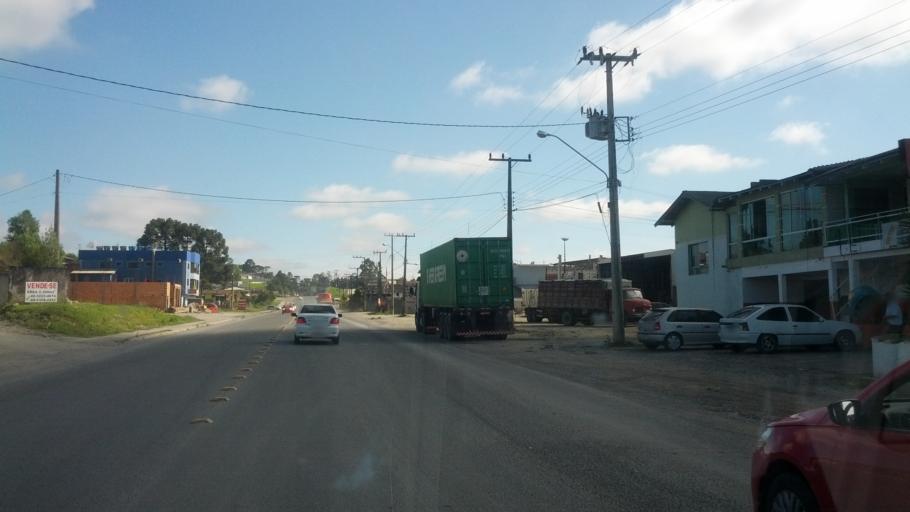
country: BR
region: Santa Catarina
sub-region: Otacilio Costa
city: Otacilio Costa
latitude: -27.4932
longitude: -50.1202
